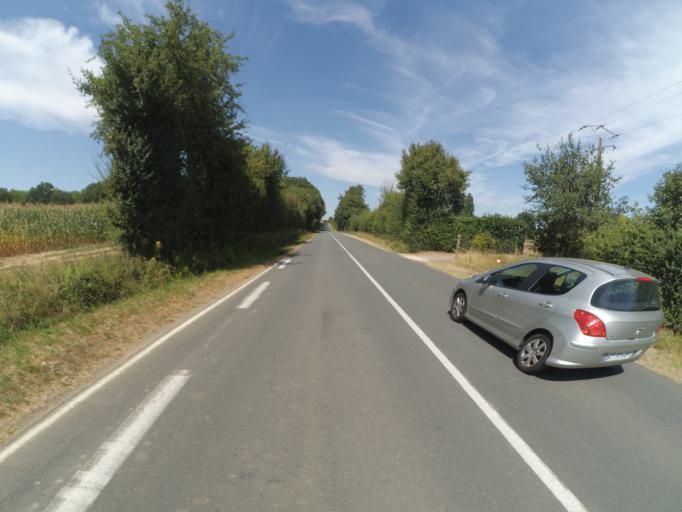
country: FR
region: Poitou-Charentes
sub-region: Departement de la Vienne
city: Usson-du-Poitou
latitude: 46.2764
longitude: 0.5178
